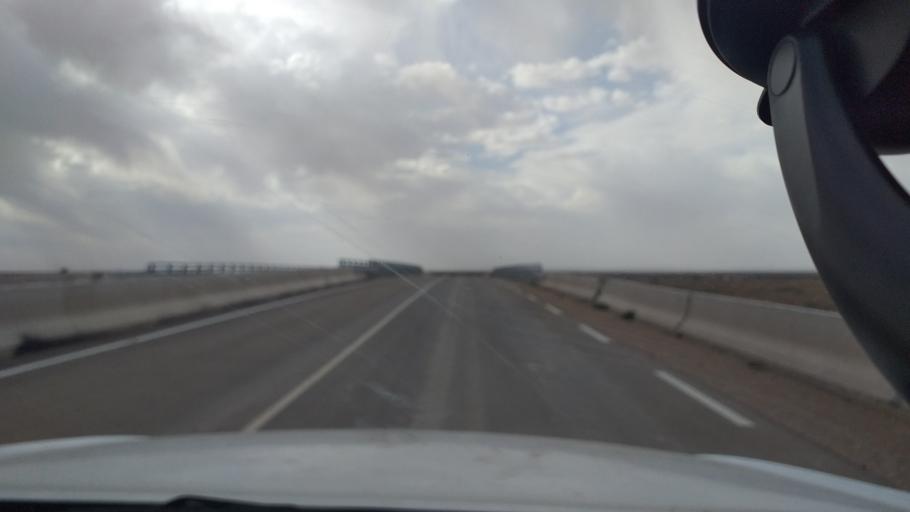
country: TN
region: Madanin
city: Medenine
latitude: 33.3007
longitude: 10.6097
